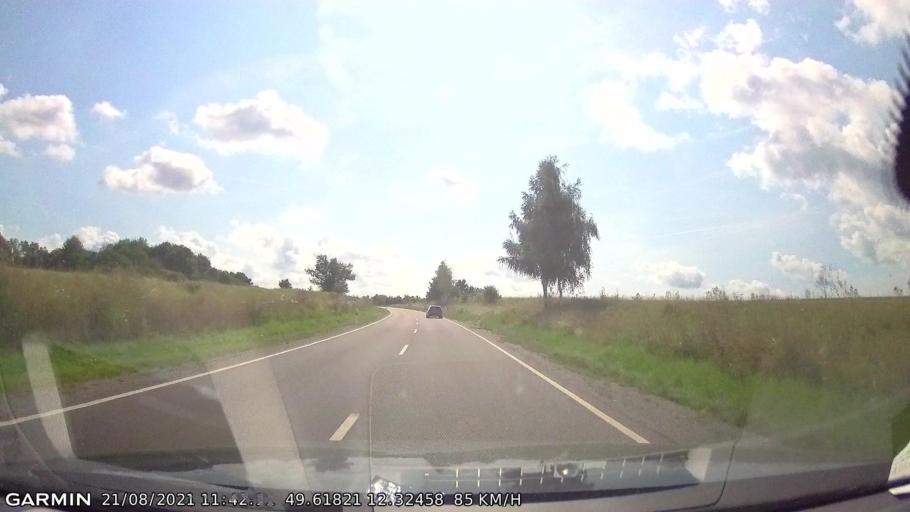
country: DE
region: Bavaria
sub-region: Upper Palatinate
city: Vohenstrauss
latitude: 49.6183
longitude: 12.3246
